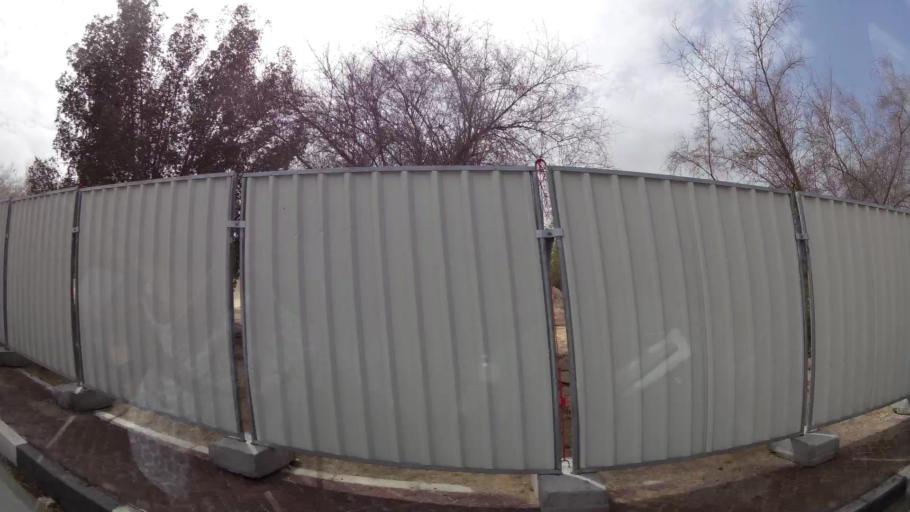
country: AE
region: Abu Dhabi
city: Abu Dhabi
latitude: 24.3957
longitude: 54.5191
